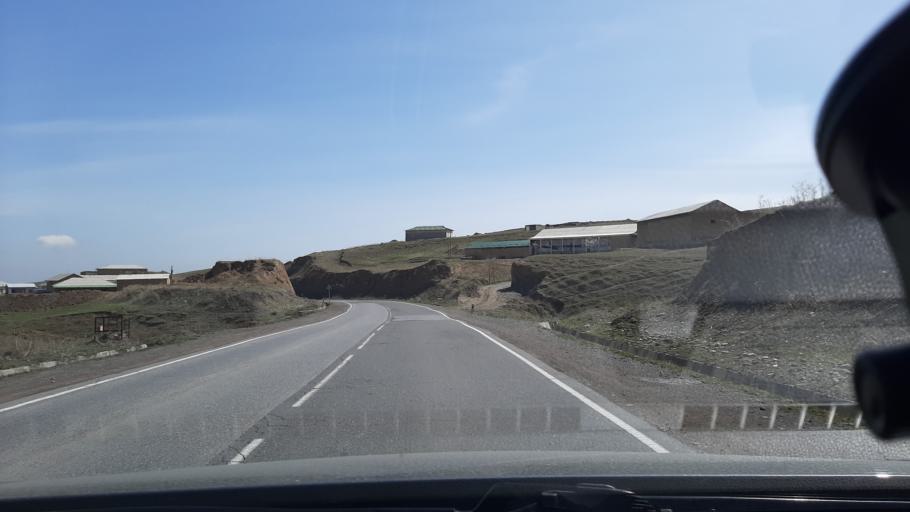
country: TJ
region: Viloyati Sughd
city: Shahriston
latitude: 39.7625
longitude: 68.8121
